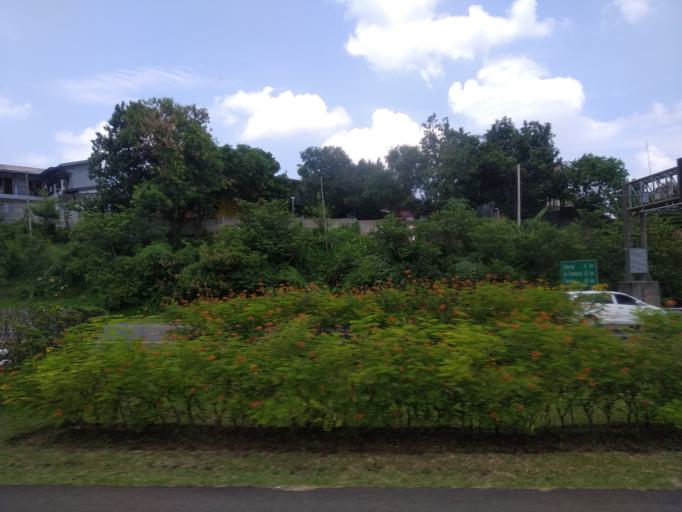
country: ID
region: West Java
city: Bogor
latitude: -6.5996
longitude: 106.8143
